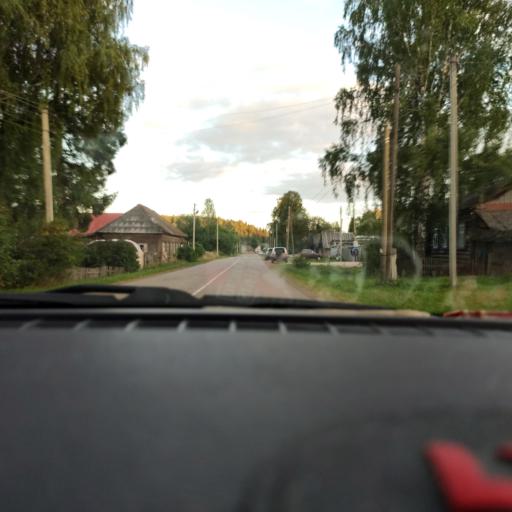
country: RU
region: Perm
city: Ocher
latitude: 57.9467
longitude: 54.8117
